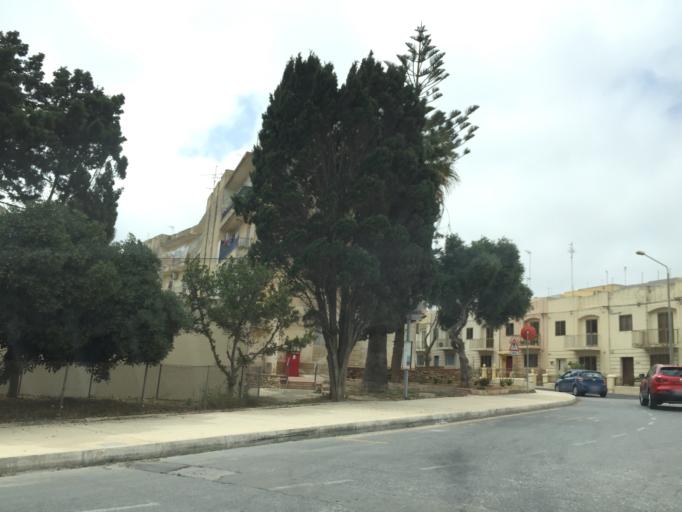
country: MT
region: Ir-Rabat
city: Rabat
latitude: 35.8838
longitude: 14.3916
